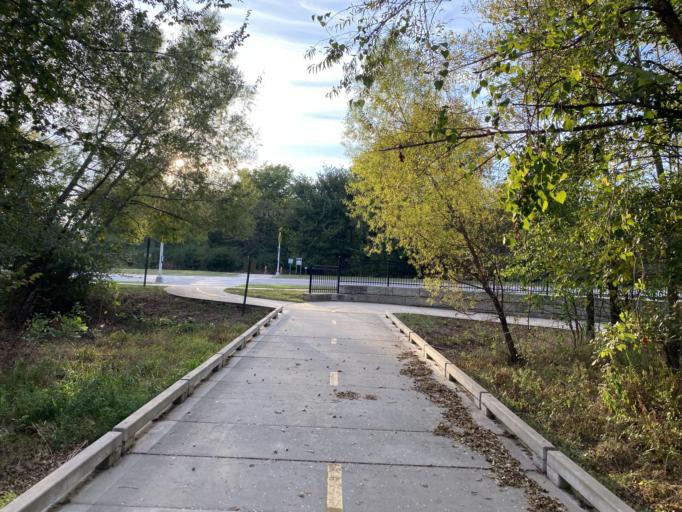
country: US
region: Arkansas
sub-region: Washington County
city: Johnson
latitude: 36.1000
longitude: -94.2121
